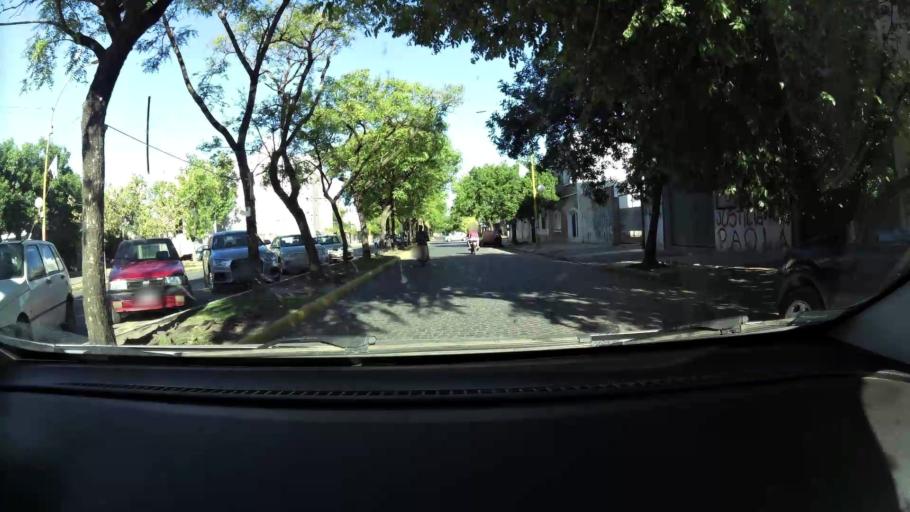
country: AR
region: Cordoba
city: San Francisco
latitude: -31.4299
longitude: -62.0914
